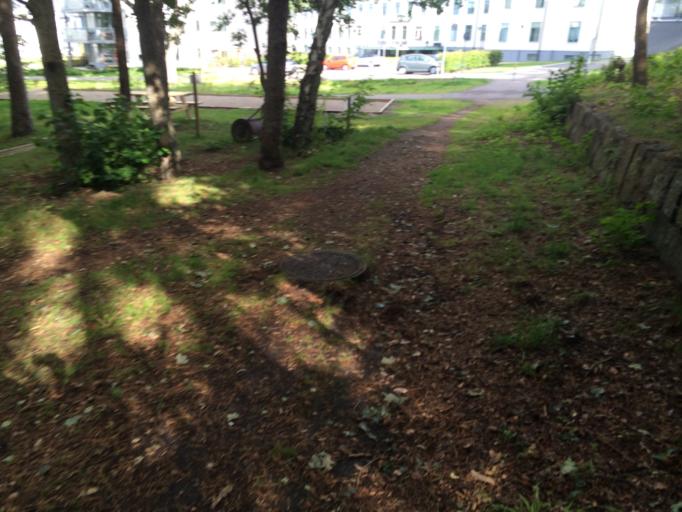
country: SE
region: Skane
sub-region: Angelholms Kommun
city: Vejbystrand
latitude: 56.3129
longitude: 12.7676
